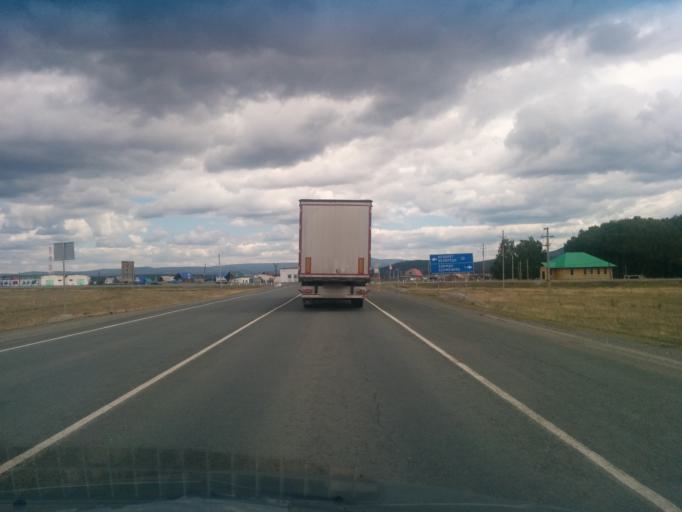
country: RU
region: Bashkortostan
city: Lomovka
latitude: 53.8807
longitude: 58.1065
